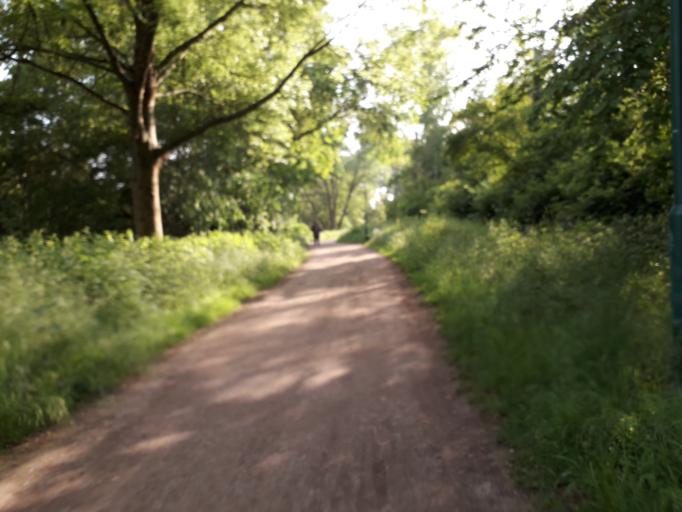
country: DE
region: Hesse
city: Pfungstadt
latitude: 49.8144
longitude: 8.6410
